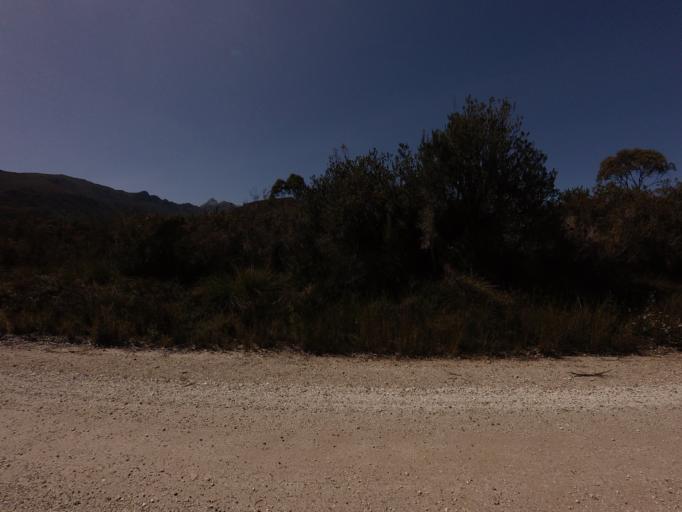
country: AU
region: Tasmania
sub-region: Huon Valley
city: Geeveston
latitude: -42.9591
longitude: 146.3616
